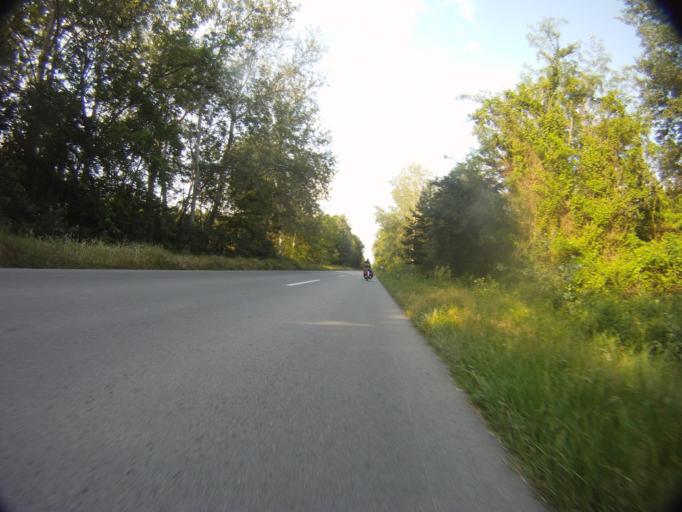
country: RO
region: Caras-Severin
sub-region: Comuna Socol
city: Socol
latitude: 44.8393
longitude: 21.2664
